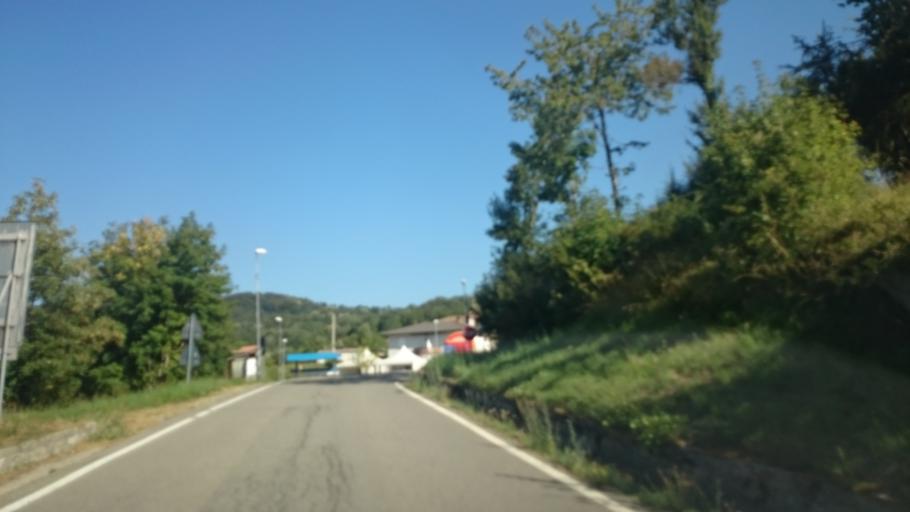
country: IT
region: Emilia-Romagna
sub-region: Provincia di Reggio Emilia
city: Villa Minozzo
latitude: 44.2974
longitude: 10.4548
